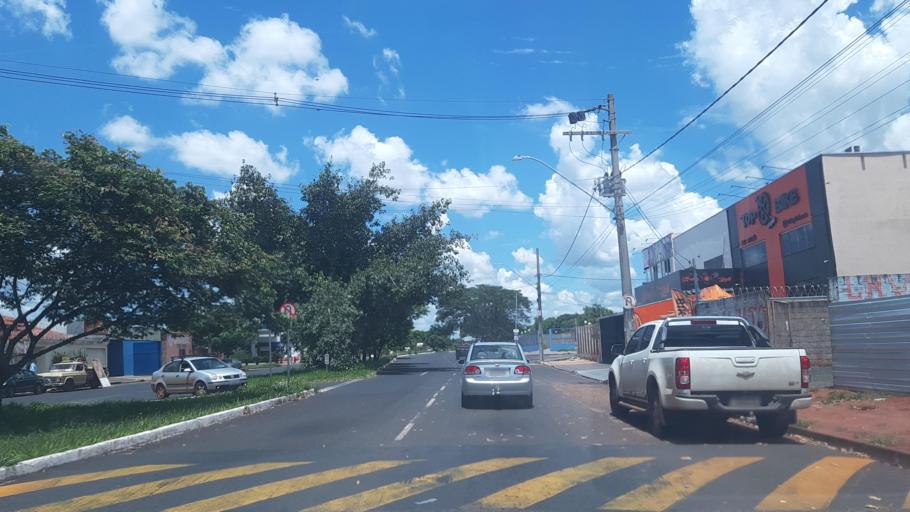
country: BR
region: Minas Gerais
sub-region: Uberlandia
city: Uberlandia
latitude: -18.9500
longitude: -48.3194
